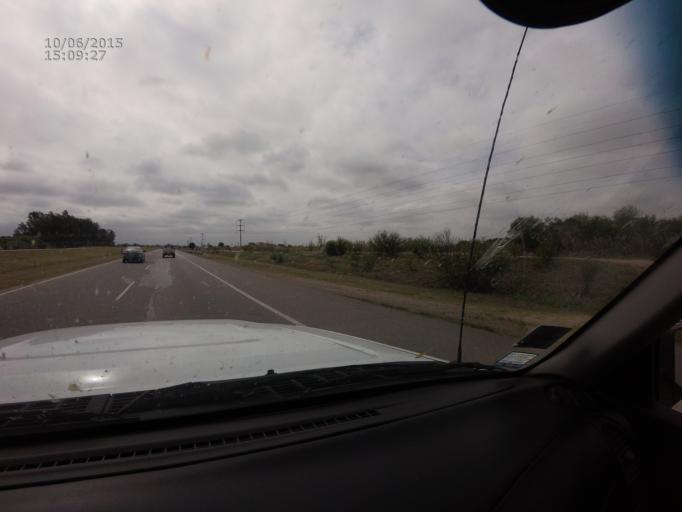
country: AR
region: Cordoba
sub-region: Departamento de Rio Segundo
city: Rio Segundo
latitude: -31.6360
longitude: -63.8701
